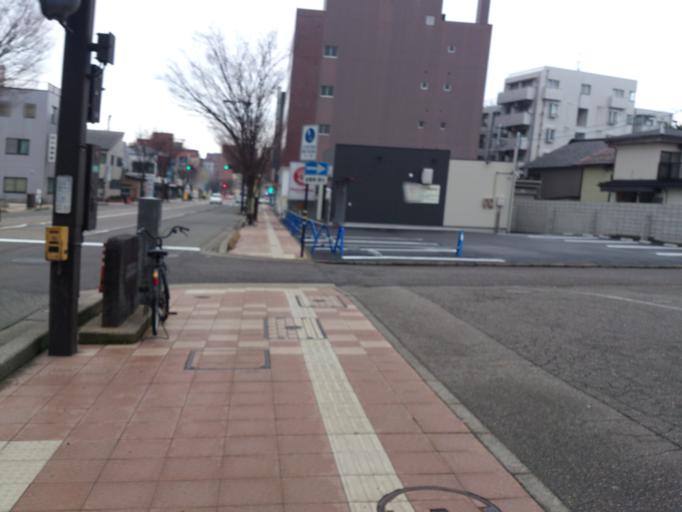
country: JP
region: Ishikawa
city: Kanazawa-shi
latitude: 36.5679
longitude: 136.6451
